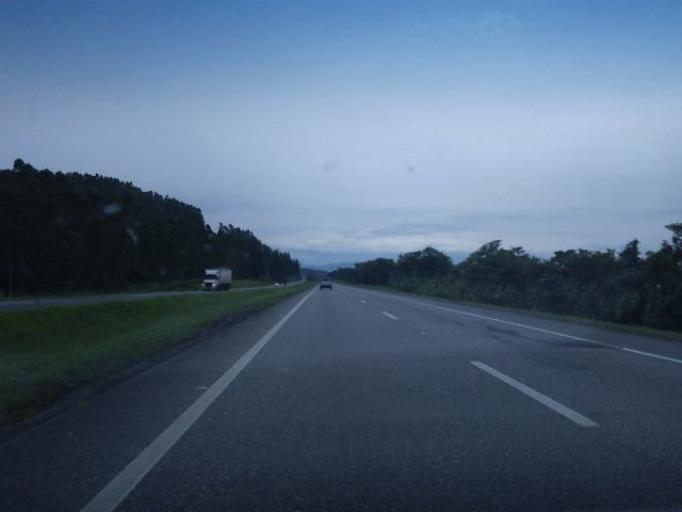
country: BR
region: Sao Paulo
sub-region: Jacupiranga
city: Jacupiranga
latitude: -24.7136
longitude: -48.0287
